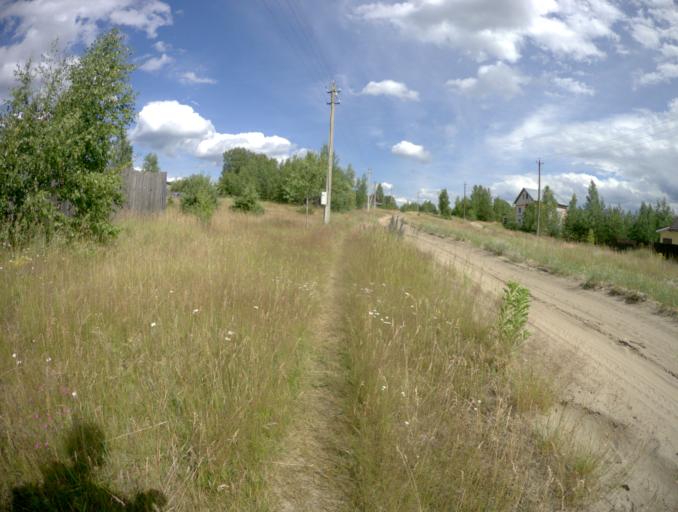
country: RU
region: Nizjnij Novgorod
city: Frolishchi
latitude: 56.4182
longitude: 42.6457
